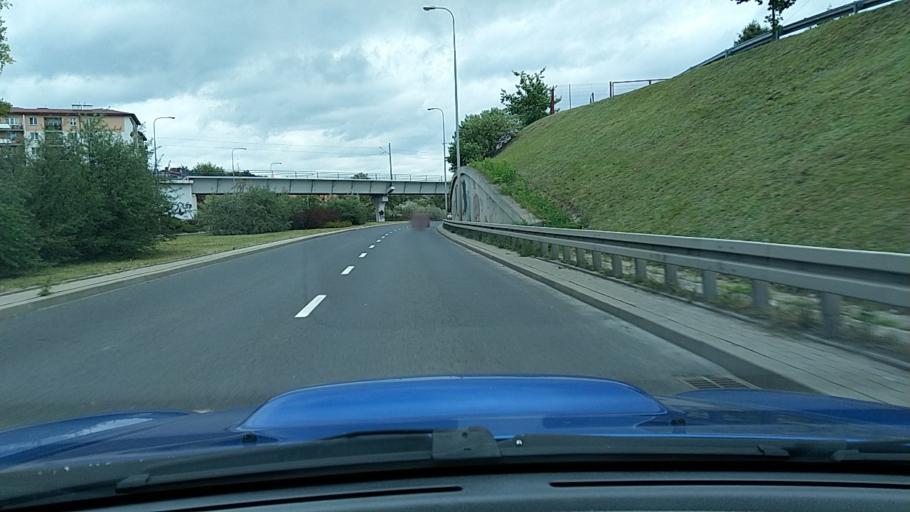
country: PL
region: Warmian-Masurian Voivodeship
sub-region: Olsztyn
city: Kortowo
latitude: 53.7766
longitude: 20.4601
